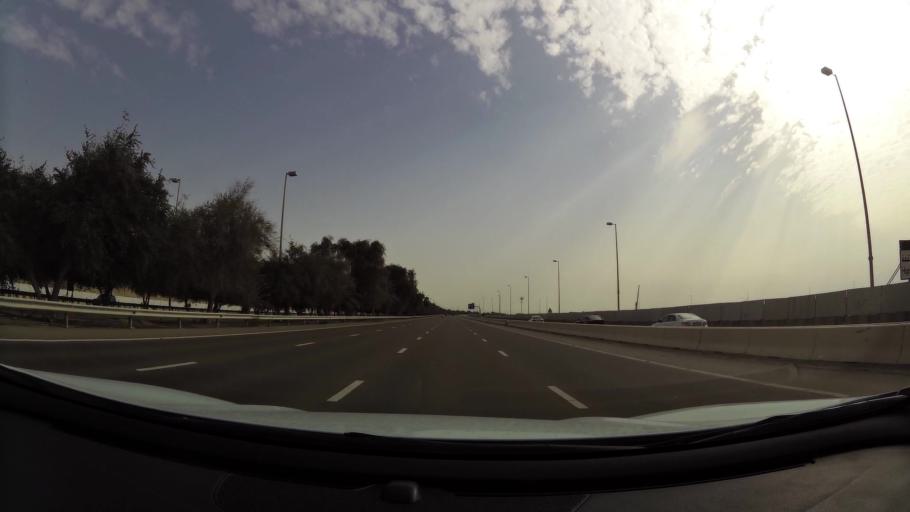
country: AE
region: Abu Dhabi
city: Abu Dhabi
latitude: 24.4269
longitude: 54.6775
